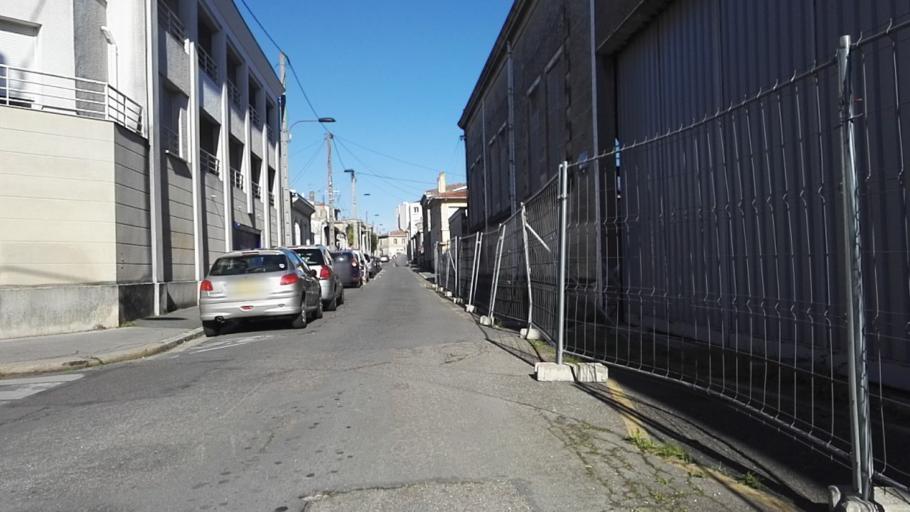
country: FR
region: Aquitaine
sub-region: Departement de la Gironde
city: Bordeaux
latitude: 44.8345
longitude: -0.6016
